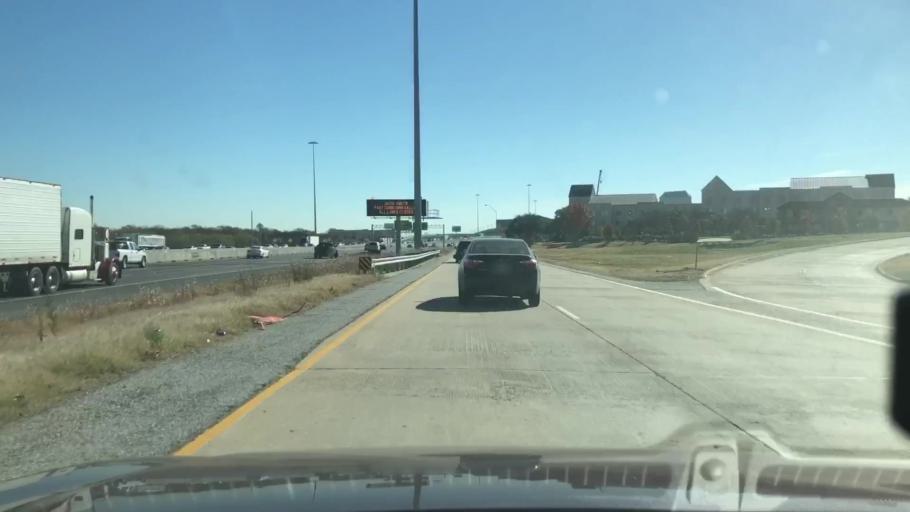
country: US
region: Texas
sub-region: Dallas County
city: Farmers Branch
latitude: 32.8860
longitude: -96.9553
